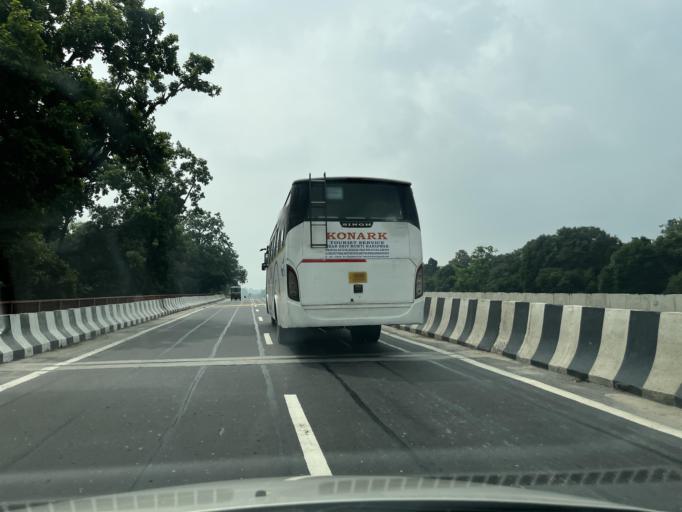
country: IN
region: Uttarakhand
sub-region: Dehradun
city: Raiwala
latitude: 30.0679
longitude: 78.2077
